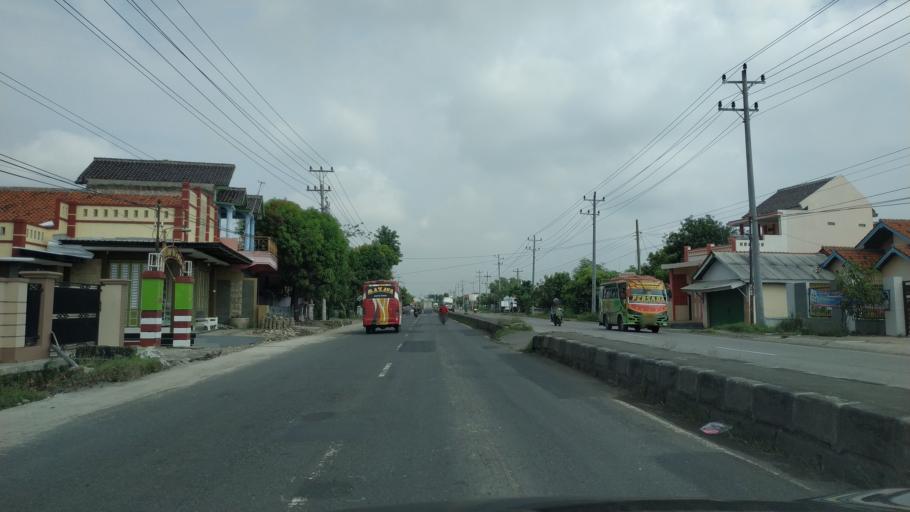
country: ID
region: Central Java
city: Bulakamba
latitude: -6.8736
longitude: 108.9139
